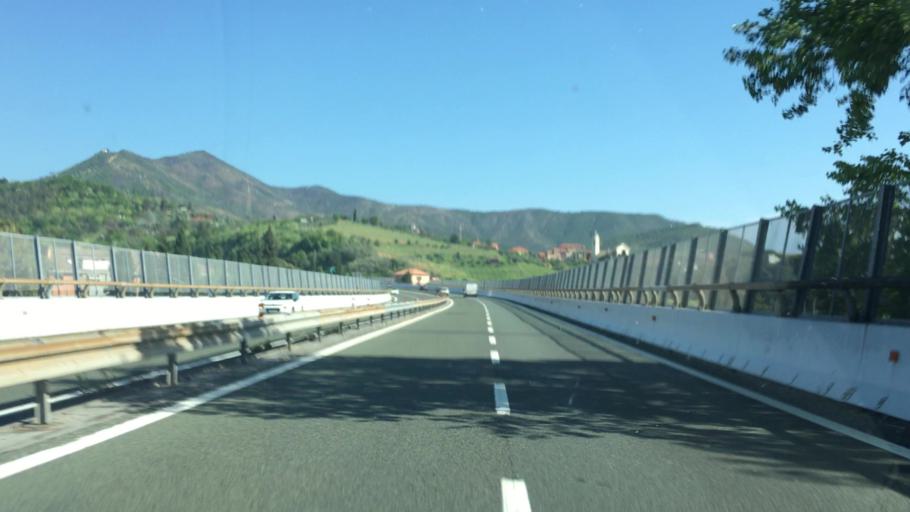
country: IT
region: Liguria
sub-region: Provincia di Genova
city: Casarza Ligure
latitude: 44.2705
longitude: 9.4258
